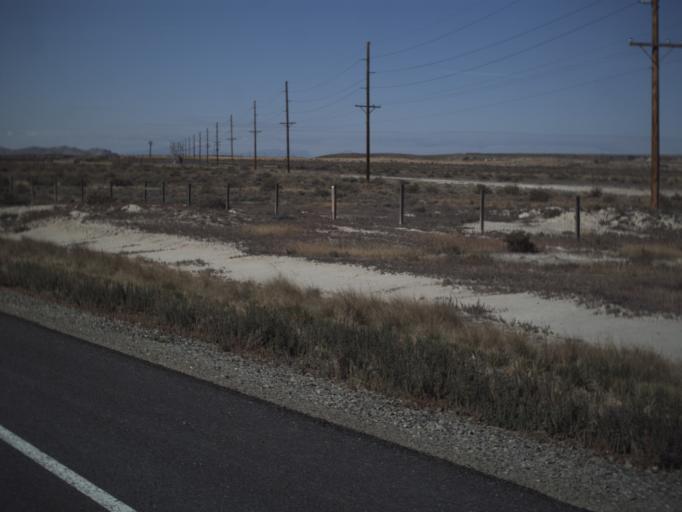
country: US
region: Utah
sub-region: Tooele County
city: Grantsville
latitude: 40.7325
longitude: -113.1168
